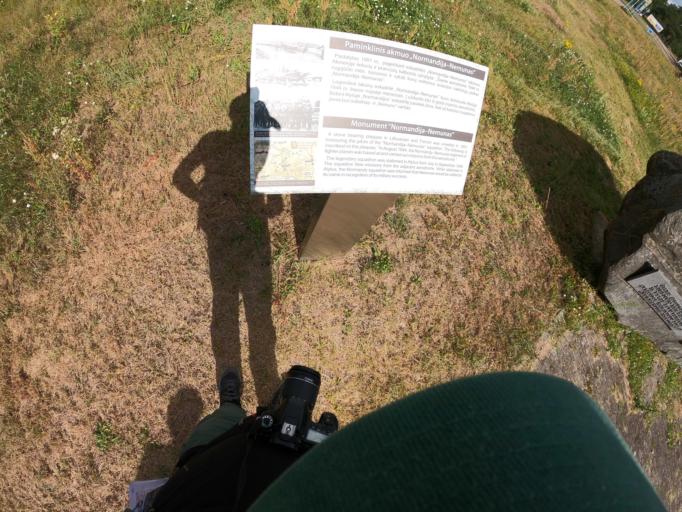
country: LT
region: Alytaus apskritis
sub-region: Alytus
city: Alytus
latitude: 54.4108
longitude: 24.0680
